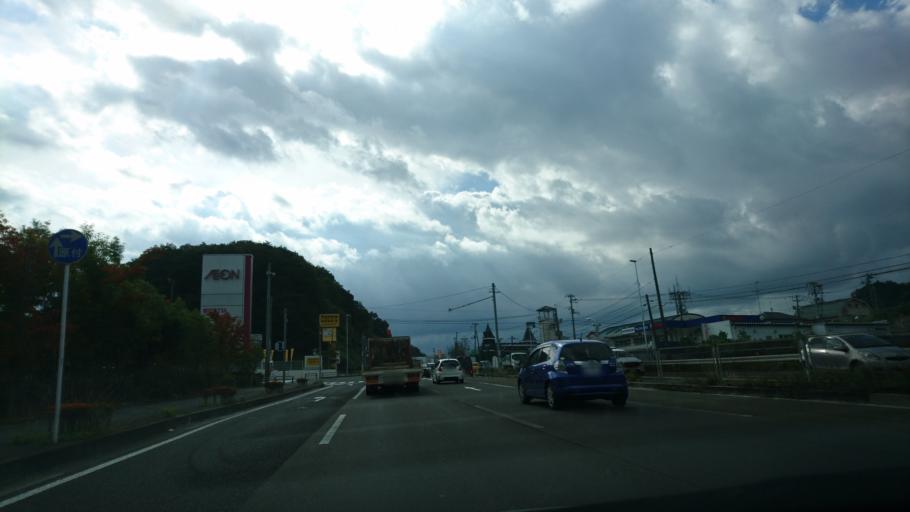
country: JP
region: Miyagi
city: Tomiya
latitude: 38.3633
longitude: 140.8732
